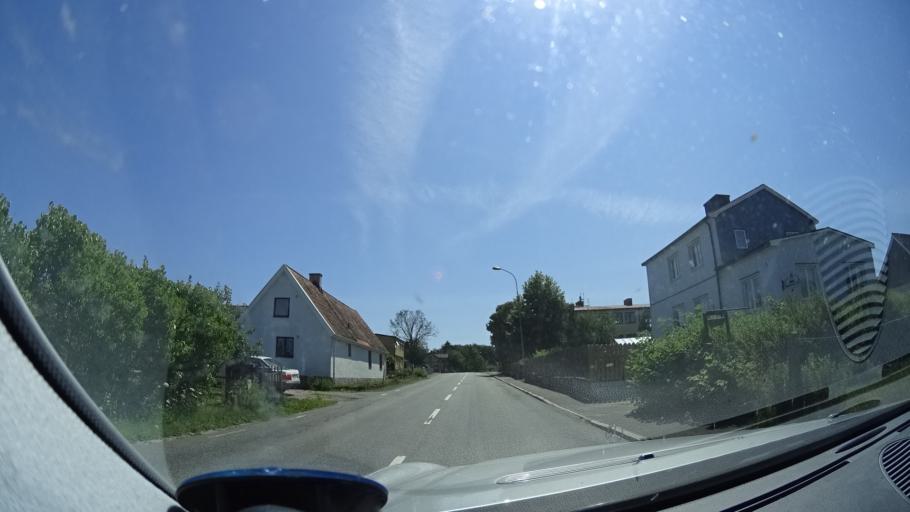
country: SE
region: Skane
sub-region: Kristianstads Kommun
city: Degeberga
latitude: 55.8862
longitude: 14.0170
